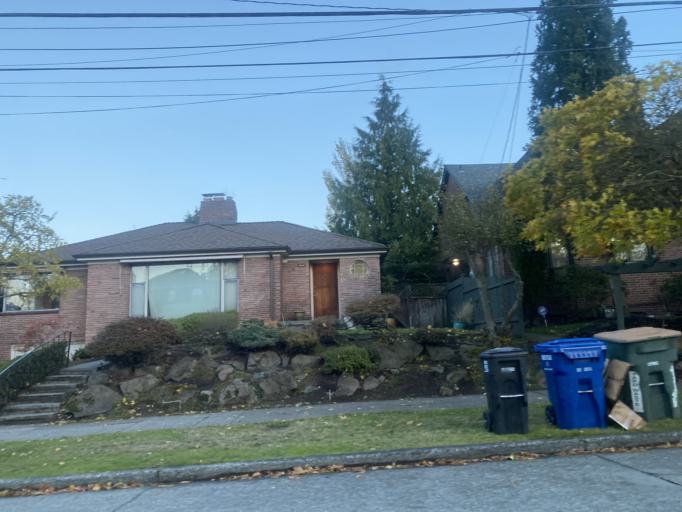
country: US
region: Washington
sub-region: King County
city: Seattle
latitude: 47.6491
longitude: -122.3929
